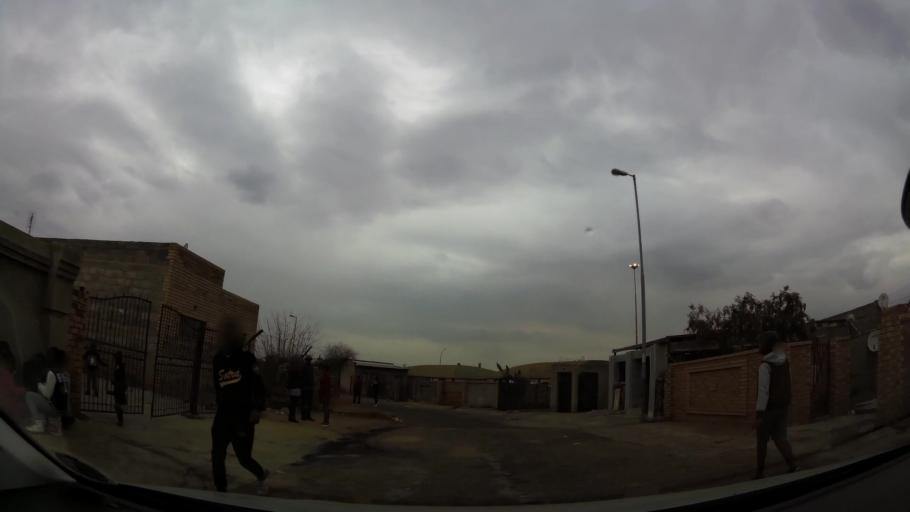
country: ZA
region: Gauteng
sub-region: City of Johannesburg Metropolitan Municipality
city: Soweto
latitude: -26.2554
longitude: 27.8728
